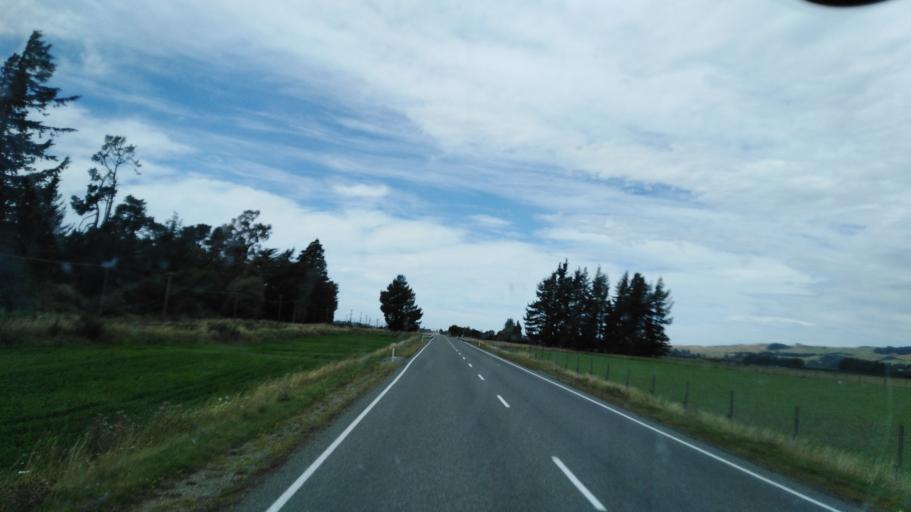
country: NZ
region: Canterbury
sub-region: Selwyn District
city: Darfield
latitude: -43.3562
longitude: 171.9626
